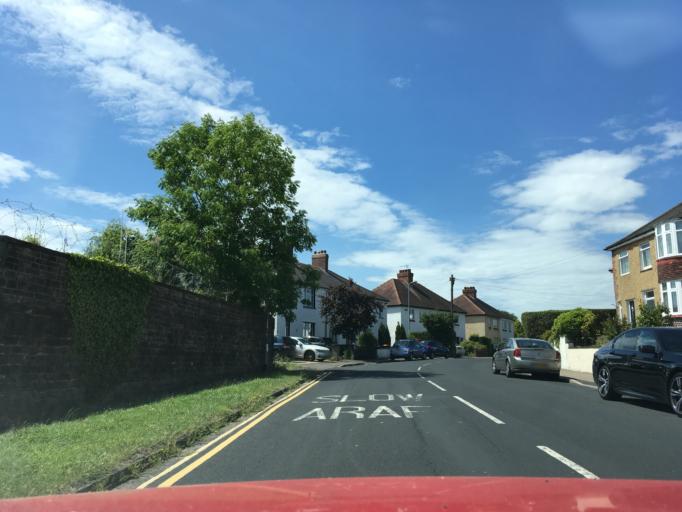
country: GB
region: Wales
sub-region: Newport
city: Newport
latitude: 51.5952
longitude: -3.0091
